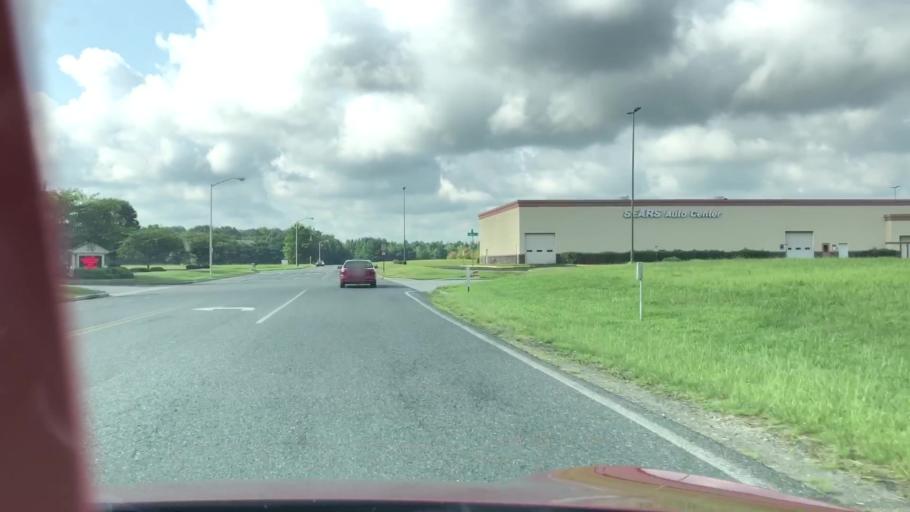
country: US
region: Maryland
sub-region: Wicomico County
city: Salisbury
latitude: 38.4014
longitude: -75.5626
